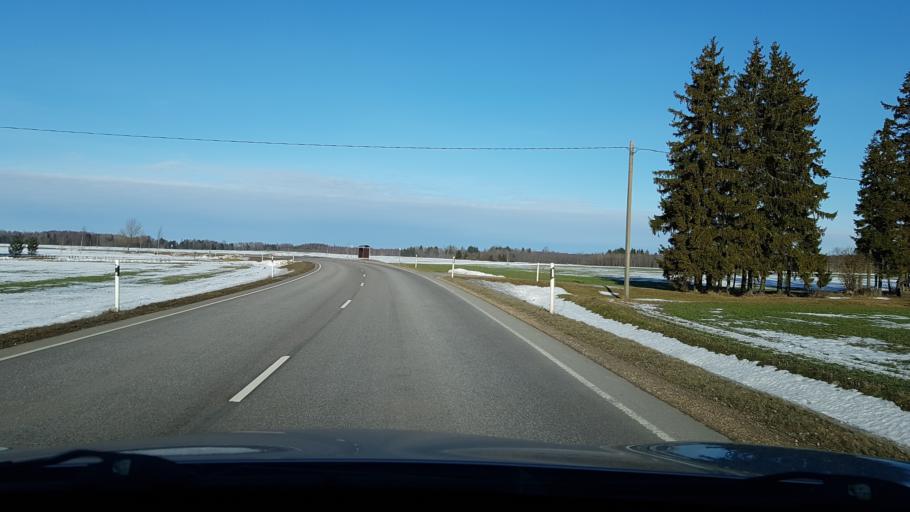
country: EE
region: Jogevamaa
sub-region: Poltsamaa linn
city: Poltsamaa
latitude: 58.6351
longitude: 25.7753
